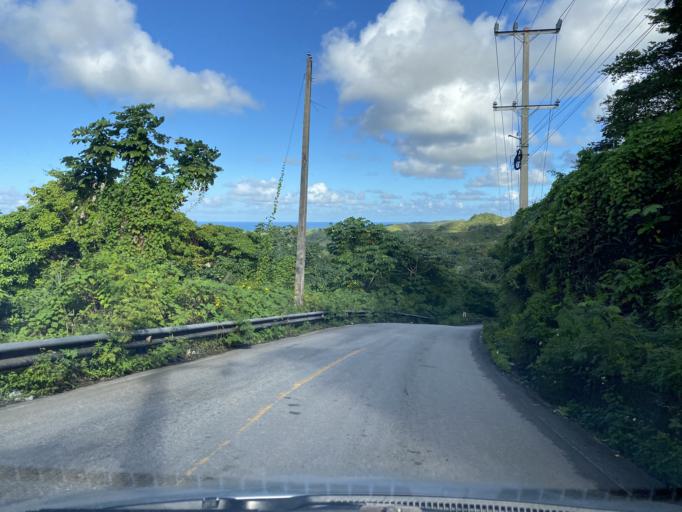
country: DO
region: Samana
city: Las Terrenas
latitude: 19.2872
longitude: -69.5522
